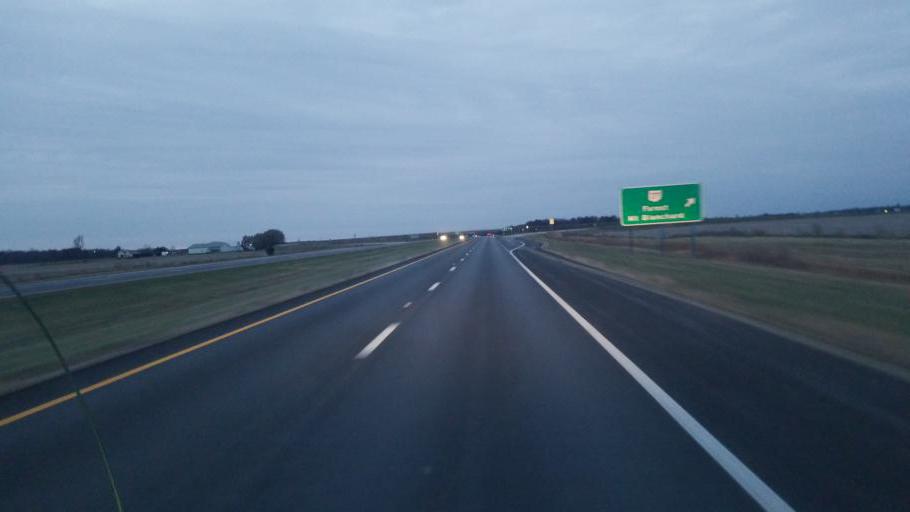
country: US
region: Ohio
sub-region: Hardin County
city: Forest
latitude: 40.8259
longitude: -83.5120
